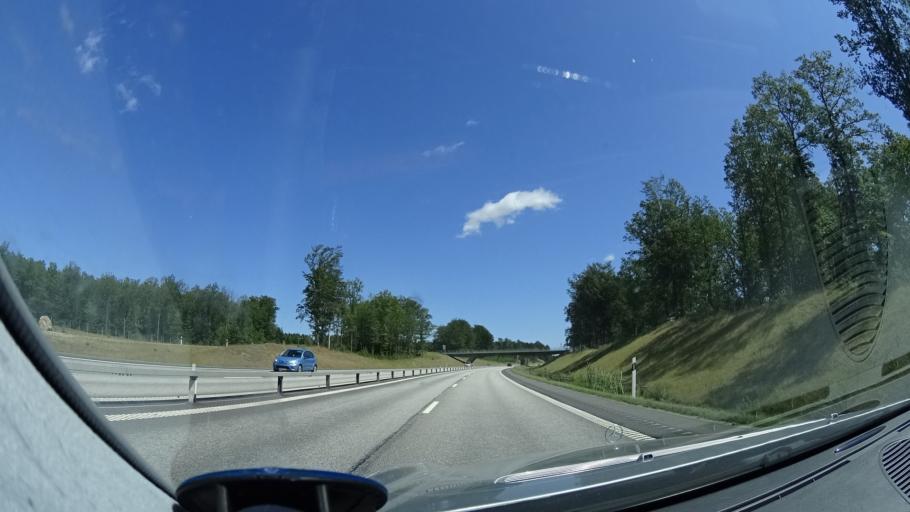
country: SE
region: Skane
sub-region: Horby Kommun
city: Hoerby
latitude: 55.9021
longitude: 13.7308
